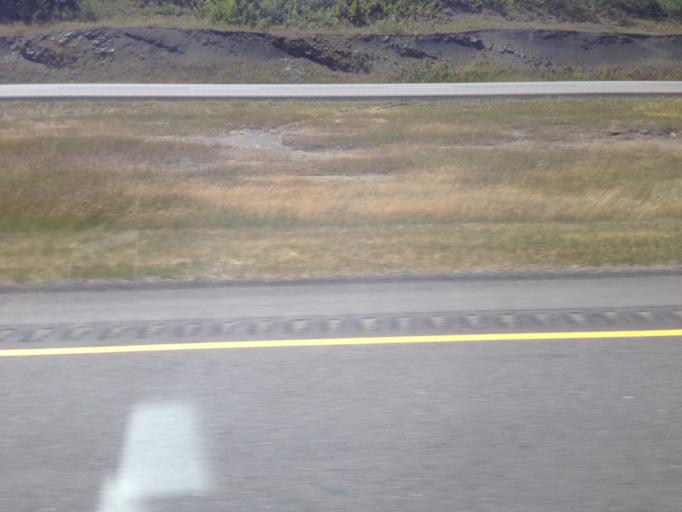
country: CA
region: Alberta
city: Cochrane
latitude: 51.0975
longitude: -114.5976
